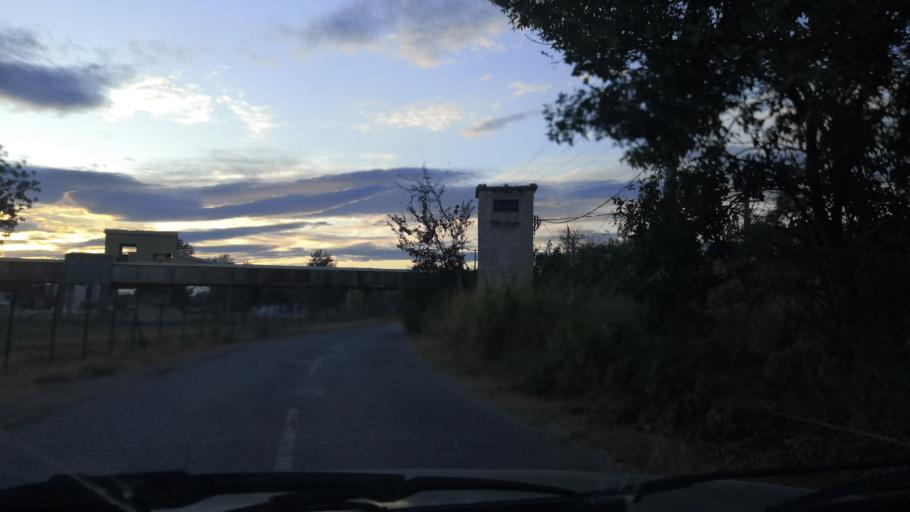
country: RO
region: Mehedinti
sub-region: Comuna Gogosu
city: Balta Verde
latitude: 44.2894
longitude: 22.6099
